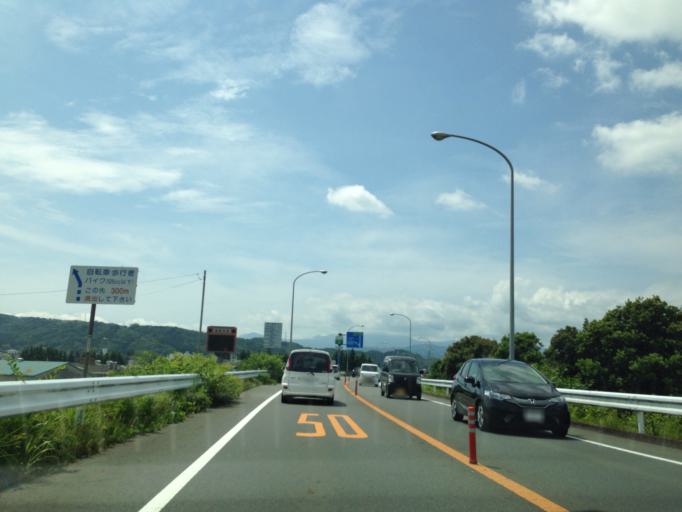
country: JP
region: Shizuoka
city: Mishima
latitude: 35.0166
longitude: 138.9400
